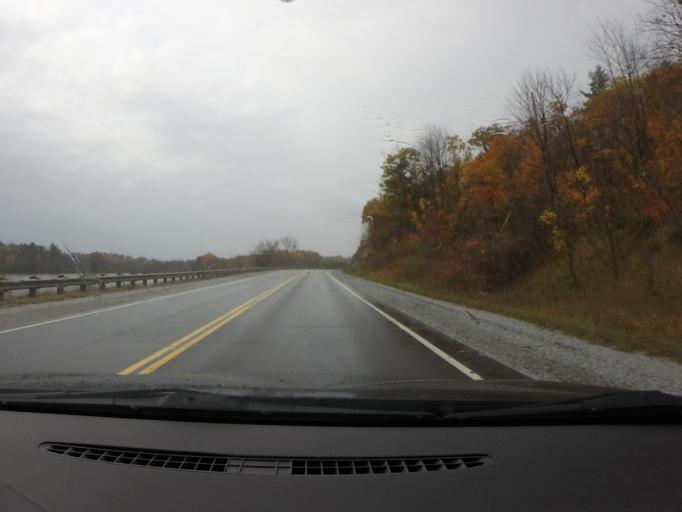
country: CA
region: Ontario
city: Perth
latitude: 44.8416
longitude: -76.5002
